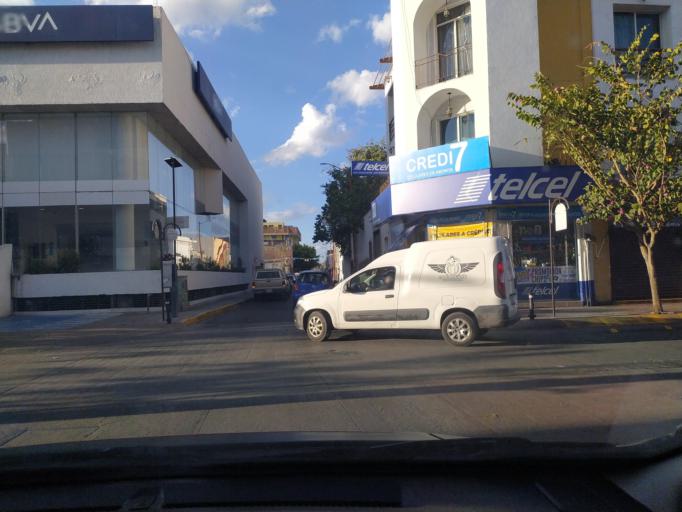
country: LA
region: Oudomxai
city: Muang La
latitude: 21.0196
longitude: 101.8559
